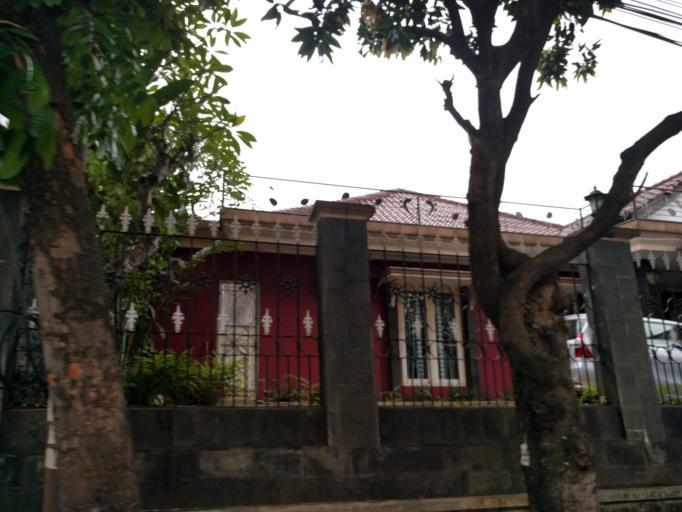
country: ID
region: West Java
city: Bogor
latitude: -6.5918
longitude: 106.8128
